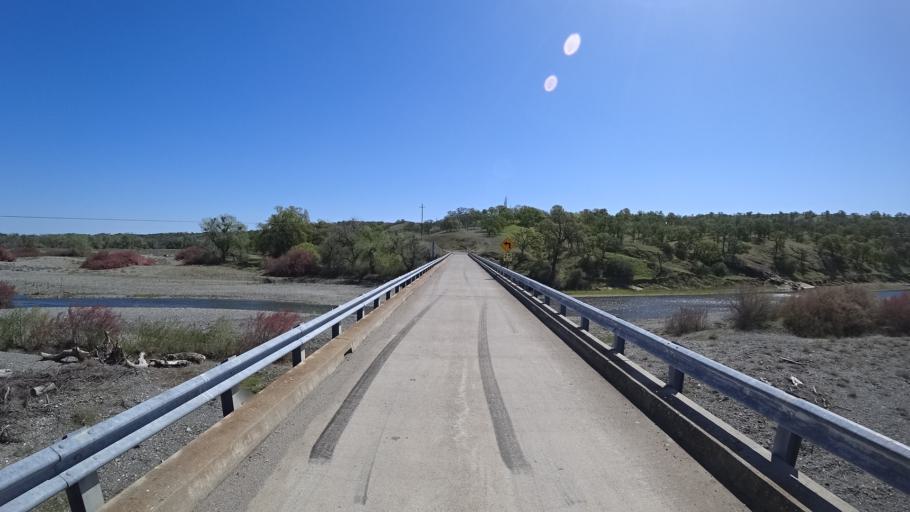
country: US
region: California
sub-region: Glenn County
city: Orland
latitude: 39.7320
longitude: -122.4145
